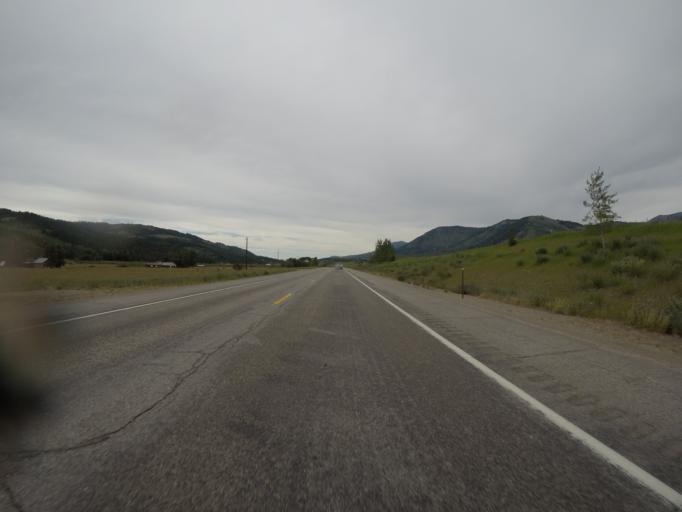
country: US
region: Wyoming
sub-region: Lincoln County
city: Afton
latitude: 42.5480
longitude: -110.8937
